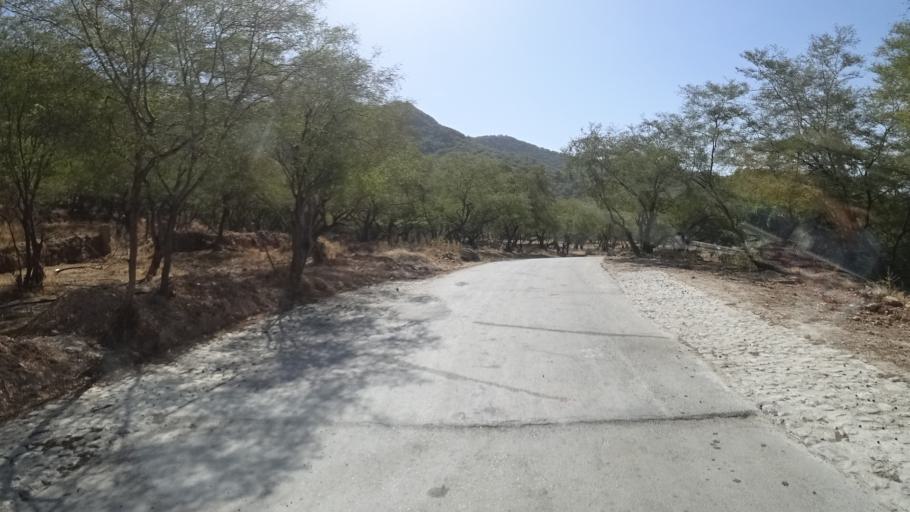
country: OM
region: Zufar
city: Salalah
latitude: 17.0826
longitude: 54.4373
